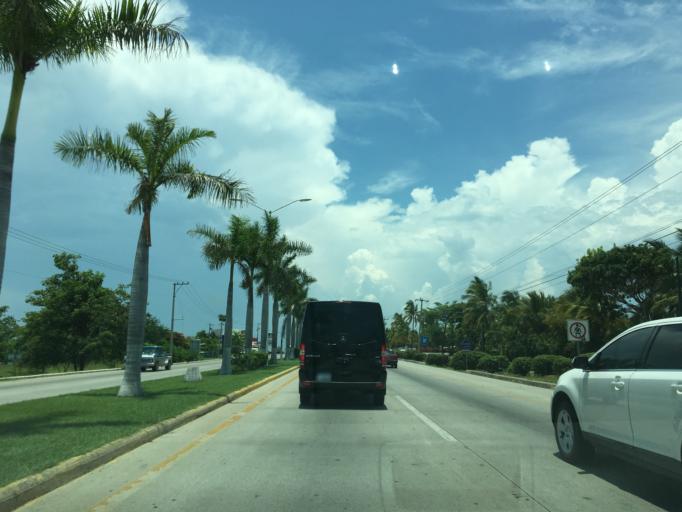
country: MX
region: Nayarit
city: Bucerias
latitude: 20.7450
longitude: -105.3059
